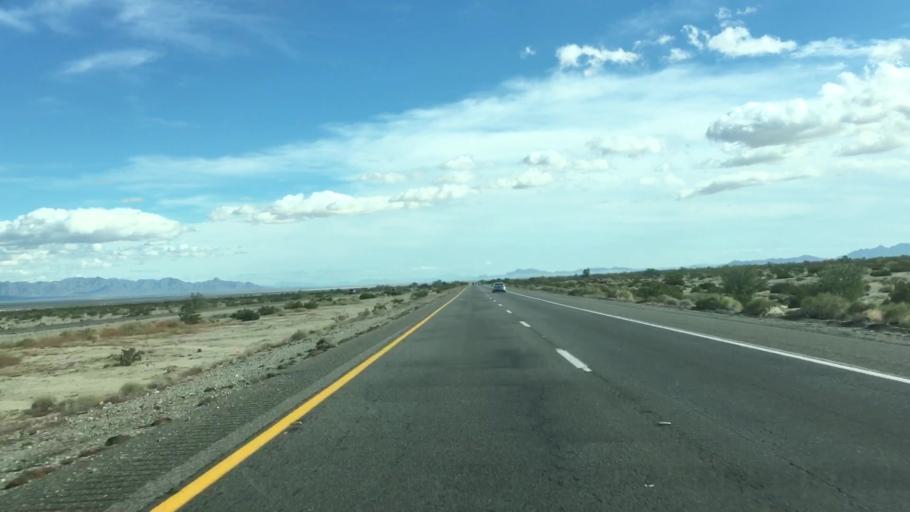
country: US
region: California
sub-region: Riverside County
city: Mesa Verde
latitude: 33.6694
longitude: -115.2000
